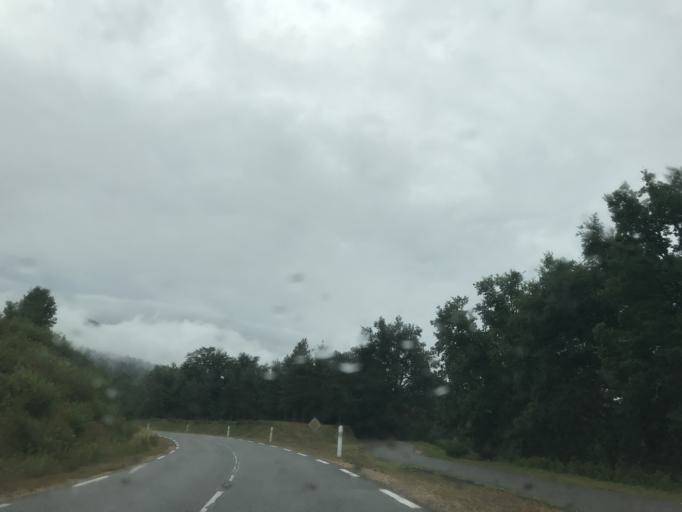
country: FR
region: Auvergne
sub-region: Departement du Puy-de-Dome
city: Job
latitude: 45.6376
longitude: 3.7078
